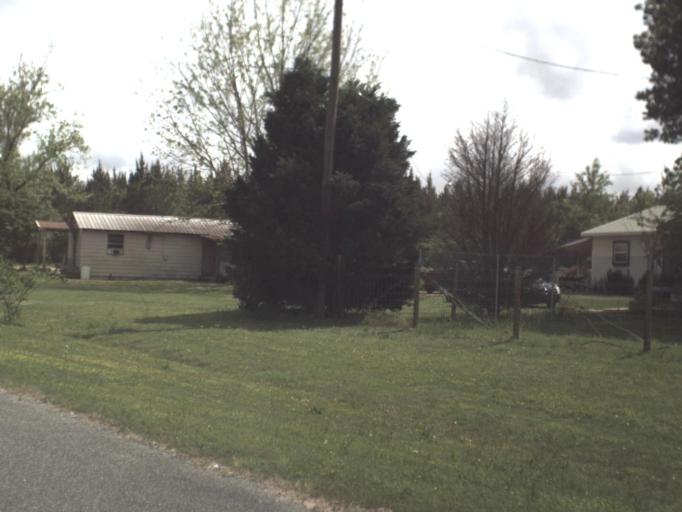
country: US
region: Florida
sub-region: Santa Rosa County
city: Wallace
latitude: 30.8116
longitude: -87.1301
